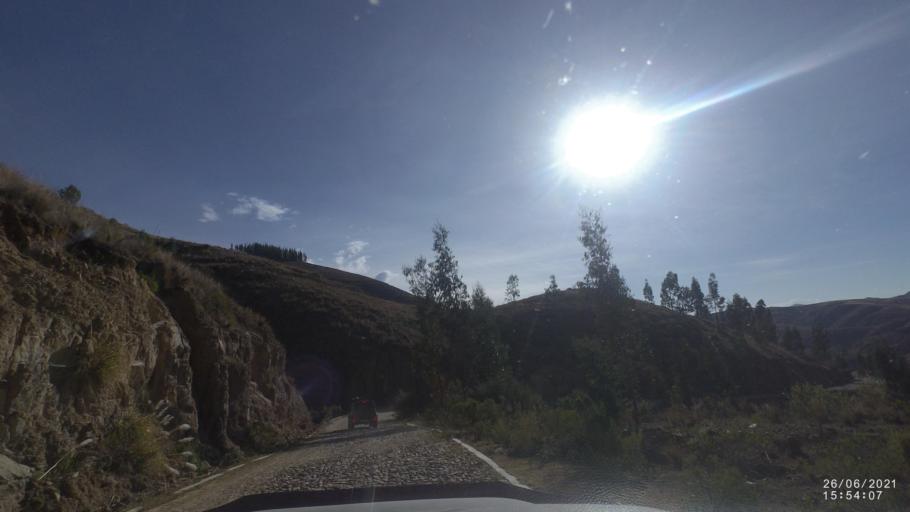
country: BO
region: Cochabamba
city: Arani
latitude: -17.8394
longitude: -65.7087
